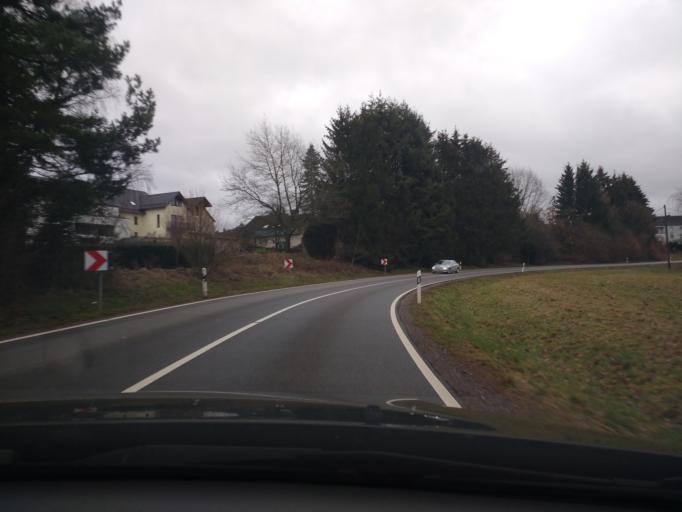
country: DE
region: Rheinland-Pfalz
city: Kell am See
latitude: 49.6317
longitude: 6.8184
